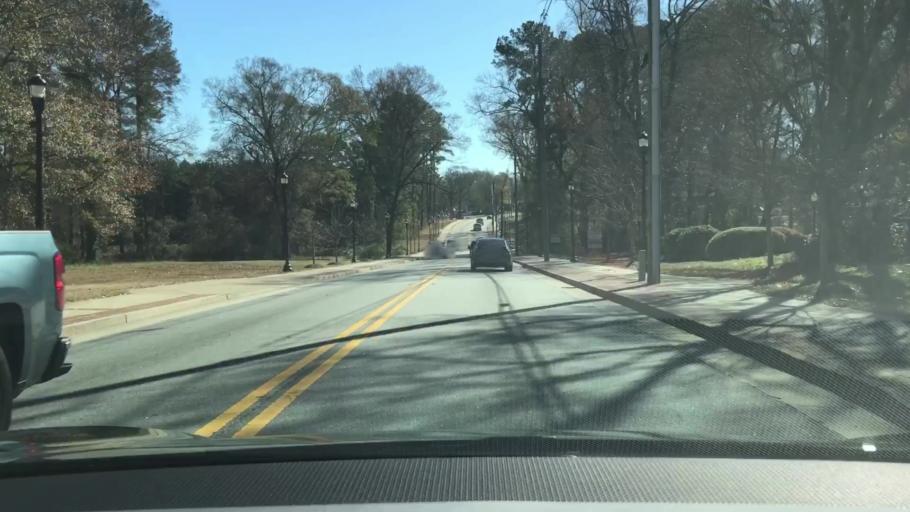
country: US
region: Georgia
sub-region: Walton County
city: Monroe
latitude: 33.7884
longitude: -83.7108
